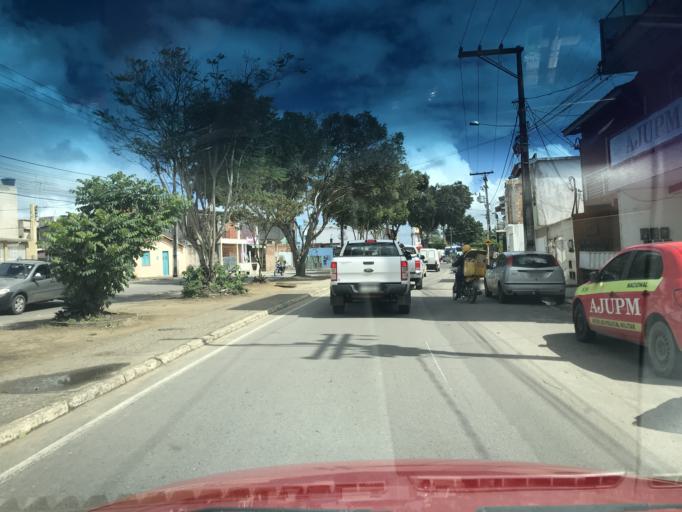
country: BR
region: Bahia
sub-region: Santo Antonio De Jesus
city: Santo Antonio de Jesus
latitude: -12.9797
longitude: -39.2775
